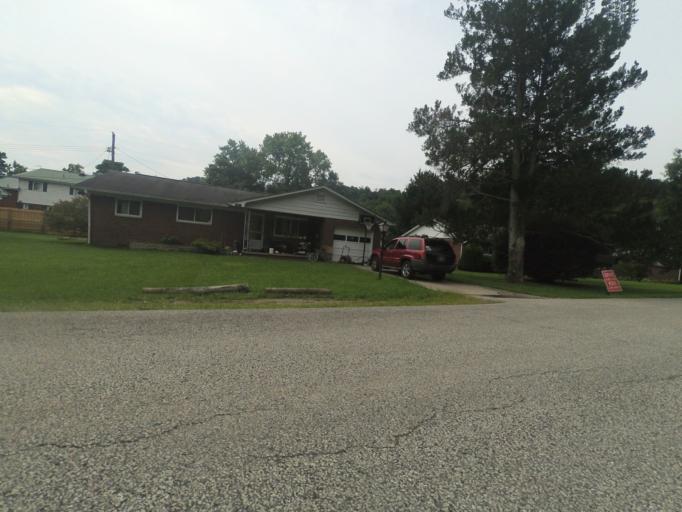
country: US
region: West Virginia
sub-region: Cabell County
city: Huntington
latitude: 38.4360
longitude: -82.4668
